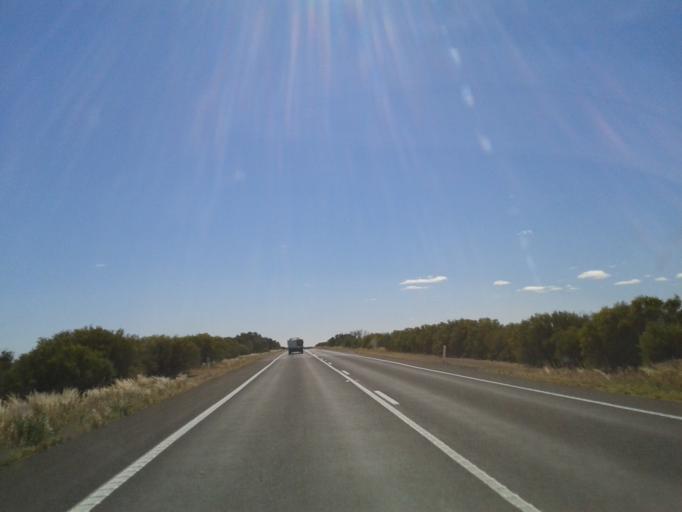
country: AU
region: New South Wales
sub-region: Wentworth
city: Dareton
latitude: -34.2637
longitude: 141.8120
